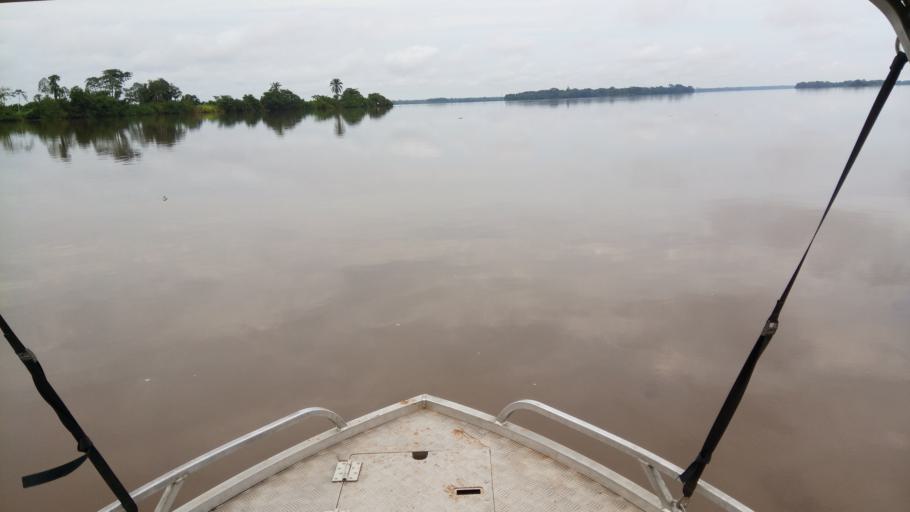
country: CD
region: Eastern Province
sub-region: Sous-Region de la Tshopo
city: Yangambi
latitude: 0.7629
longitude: 24.3169
